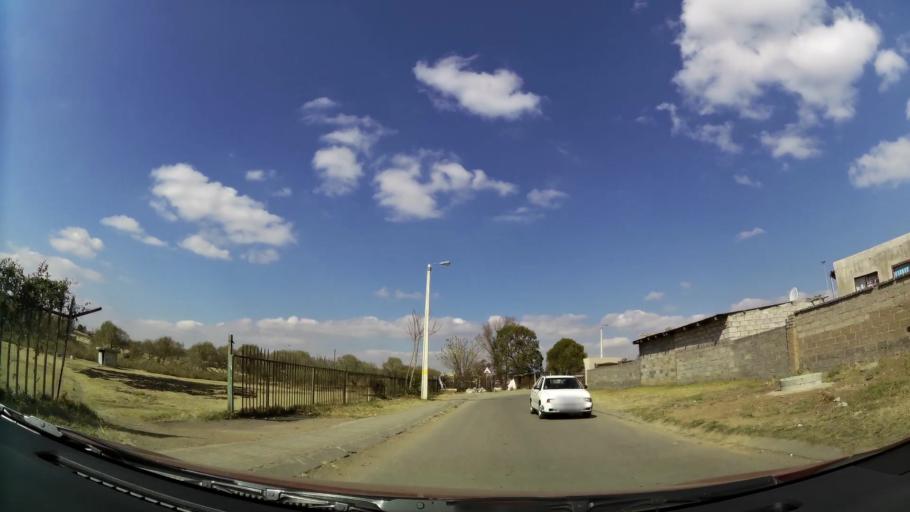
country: ZA
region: Gauteng
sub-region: Ekurhuleni Metropolitan Municipality
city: Tembisa
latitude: -26.0138
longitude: 28.2009
